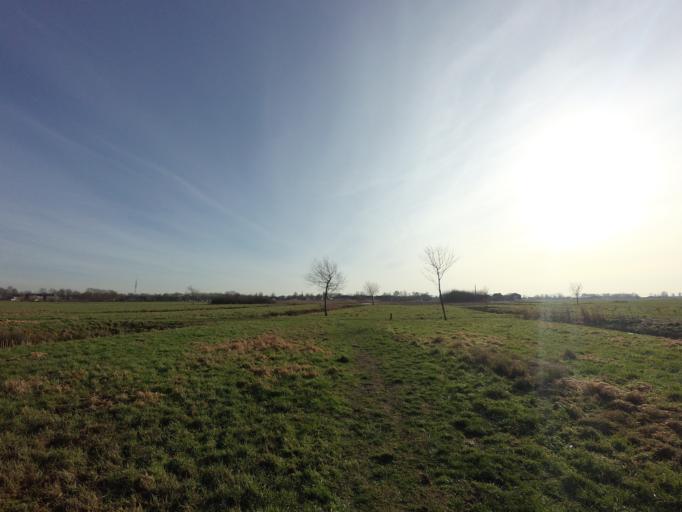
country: NL
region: Utrecht
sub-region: Gemeente Oudewater
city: Oudewater
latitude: 52.0319
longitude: 4.8567
